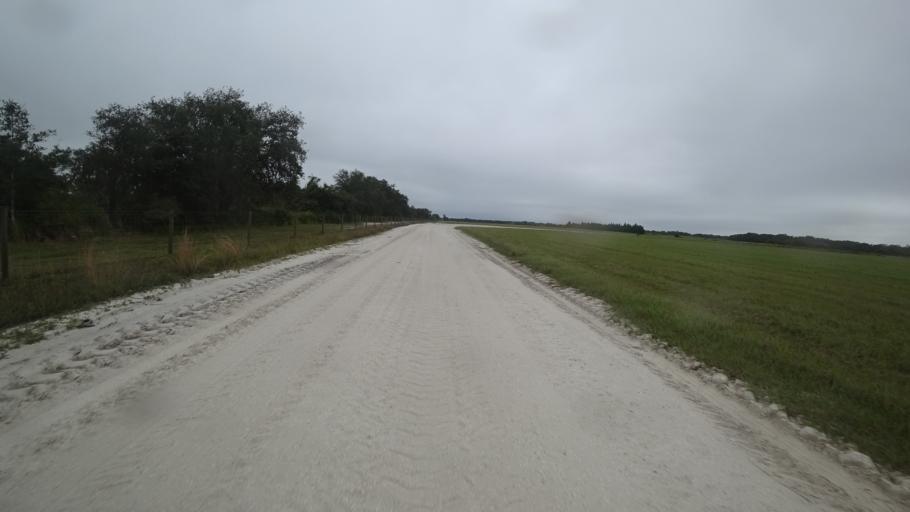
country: US
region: Florida
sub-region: Sarasota County
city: Warm Mineral Springs
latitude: 27.2881
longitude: -82.1346
